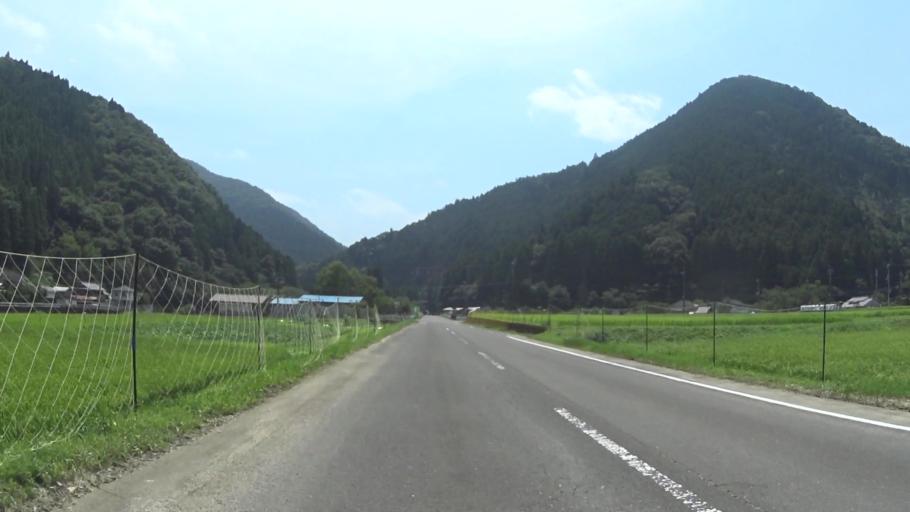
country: JP
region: Kyoto
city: Ayabe
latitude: 35.3003
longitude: 135.4259
